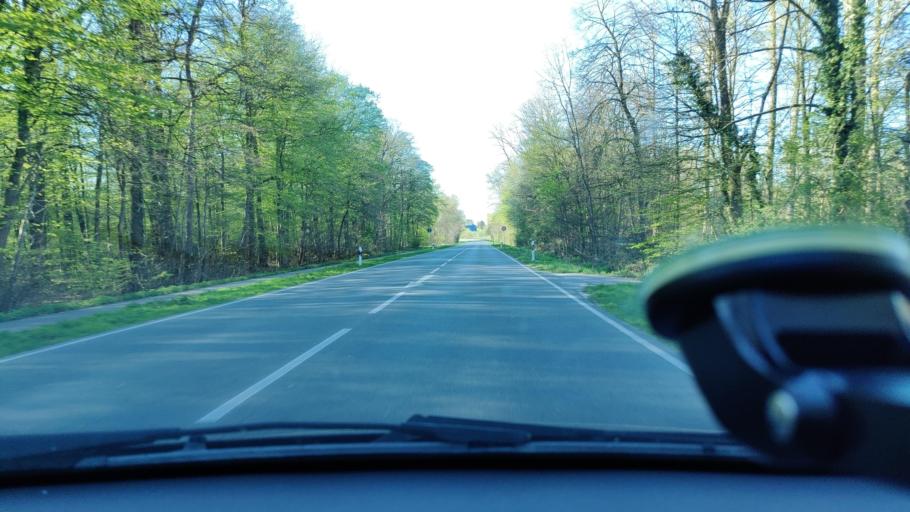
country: DE
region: North Rhine-Westphalia
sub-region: Regierungsbezirk Munster
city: Coesfeld
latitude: 51.9685
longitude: 7.1567
